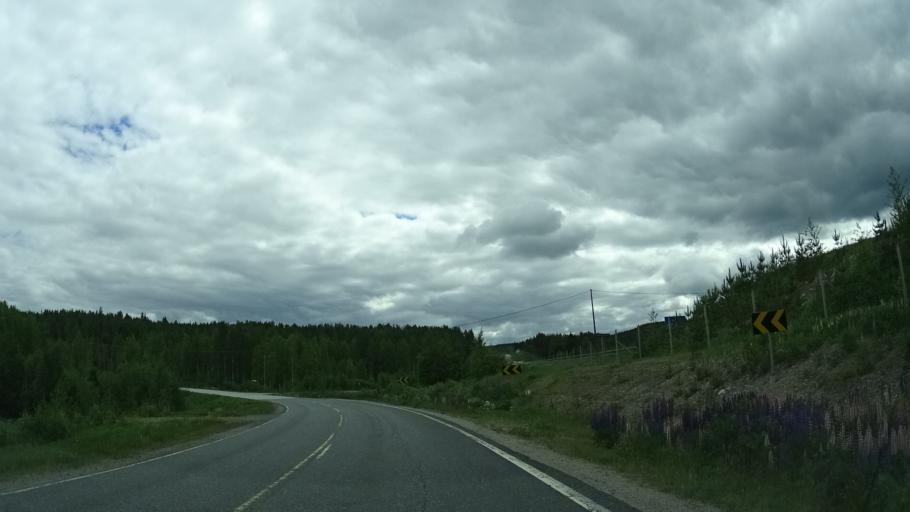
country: FI
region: Central Finland
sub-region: Jyvaeskylae
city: Toivakka
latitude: 62.0783
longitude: 26.0352
